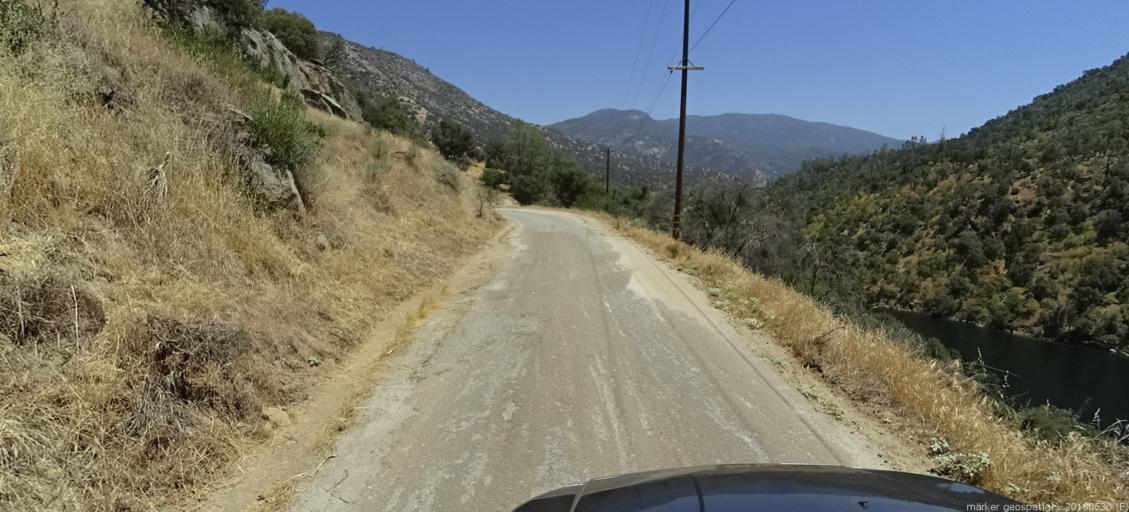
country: US
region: California
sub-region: Fresno County
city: Auberry
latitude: 37.1660
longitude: -119.4230
